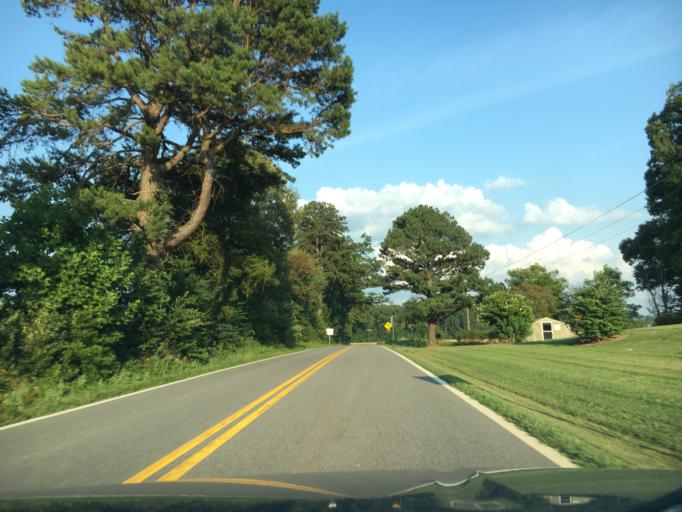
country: US
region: Virginia
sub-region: Halifax County
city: Mountain Road
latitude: 36.8288
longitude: -79.1112
